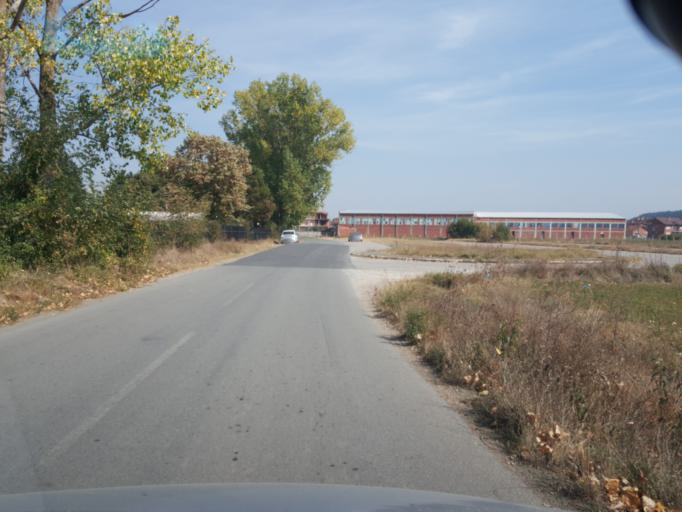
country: XK
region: Gjakova
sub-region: Komuna e Gjakoves
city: Gjakove
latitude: 42.3698
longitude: 20.4070
